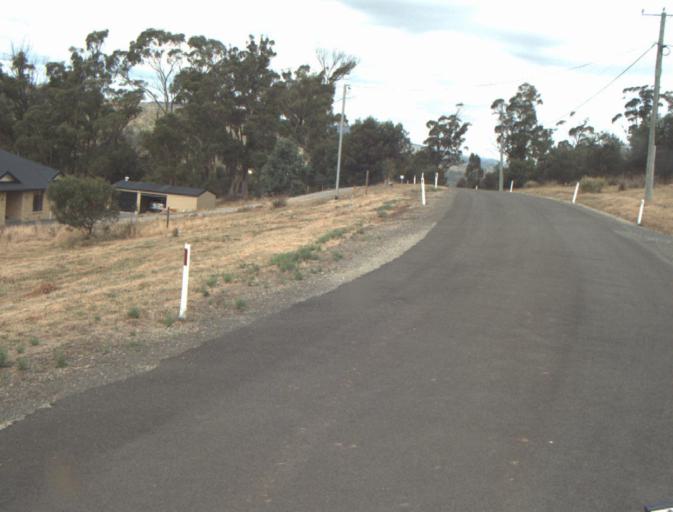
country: AU
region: Tasmania
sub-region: Launceston
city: Mayfield
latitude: -41.3028
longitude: 147.0417
